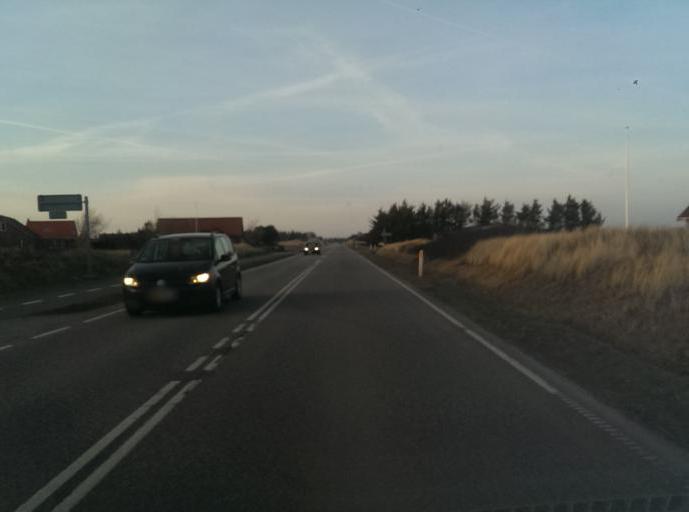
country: DK
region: Central Jutland
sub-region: Ringkobing-Skjern Kommune
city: Hvide Sande
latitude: 56.0555
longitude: 8.1203
